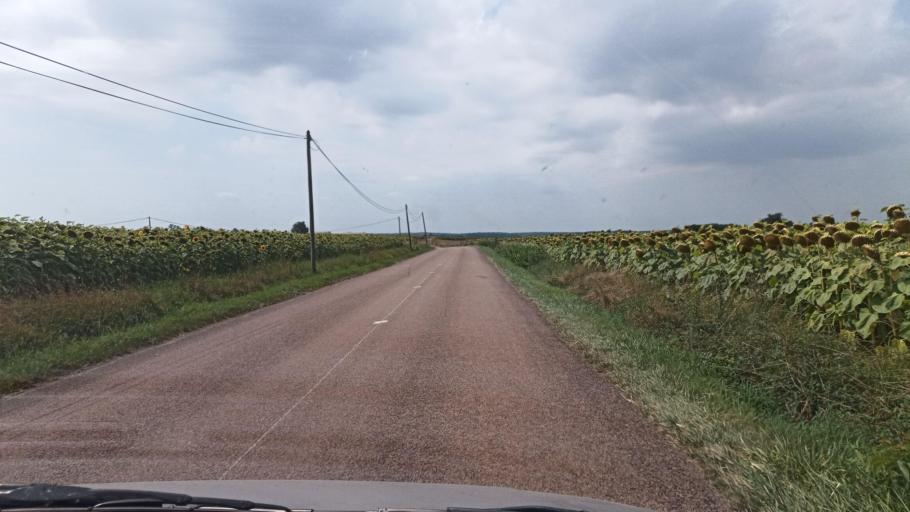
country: FR
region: Bourgogne
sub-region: Departement de l'Yonne
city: Egriselles-le-Bocage
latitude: 48.0424
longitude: 3.2035
